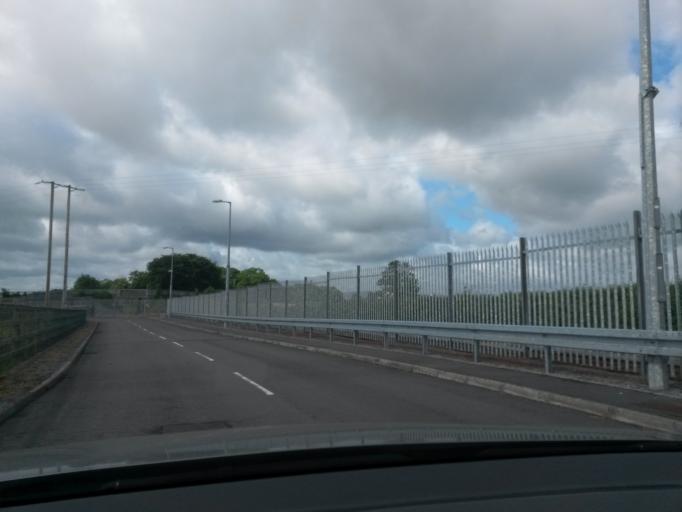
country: IE
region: Connaught
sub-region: County Galway
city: Gort
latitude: 53.1561
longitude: -8.8162
